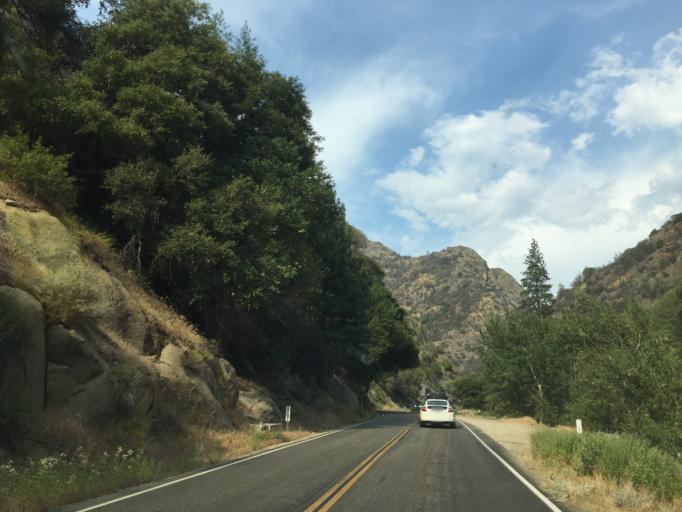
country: US
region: California
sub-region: Tulare County
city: Three Rivers
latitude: 36.8076
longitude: -118.7967
